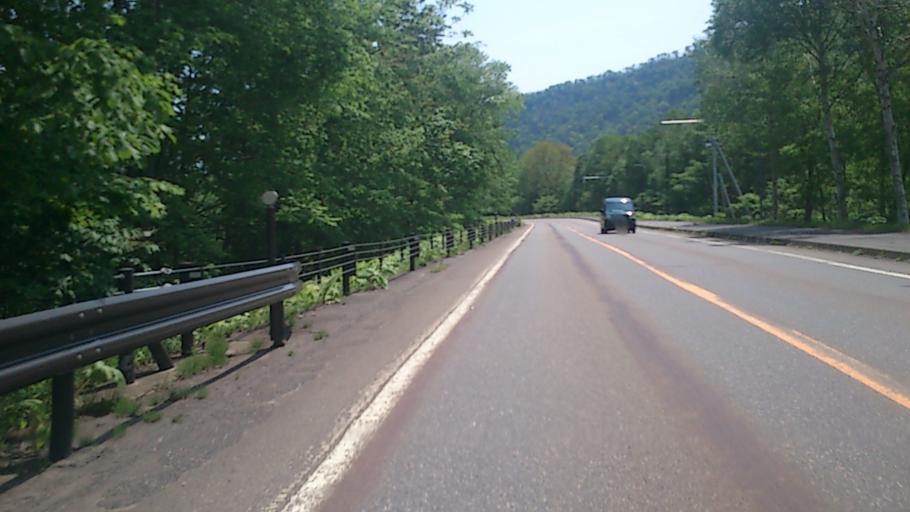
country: JP
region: Hokkaido
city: Otofuke
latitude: 43.3585
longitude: 143.2544
